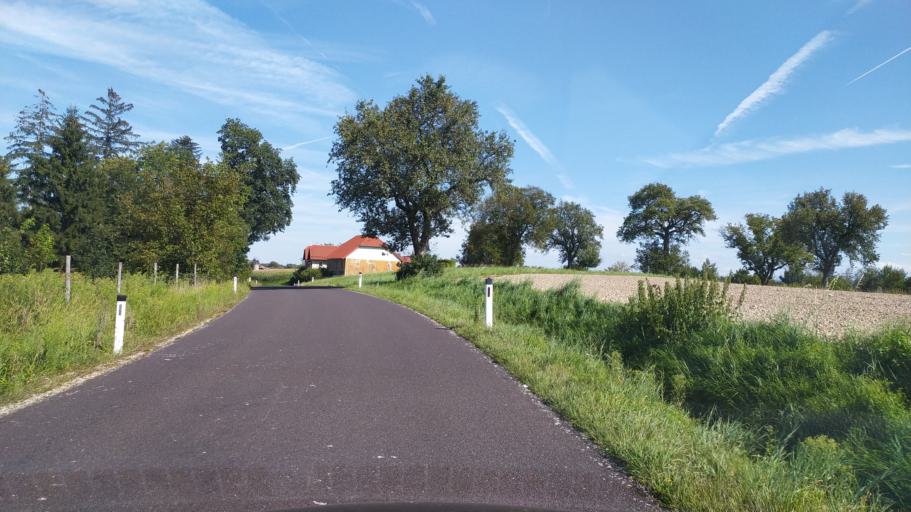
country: AT
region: Lower Austria
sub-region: Politischer Bezirk Amstetten
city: Strengberg
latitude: 48.1167
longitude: 14.6315
